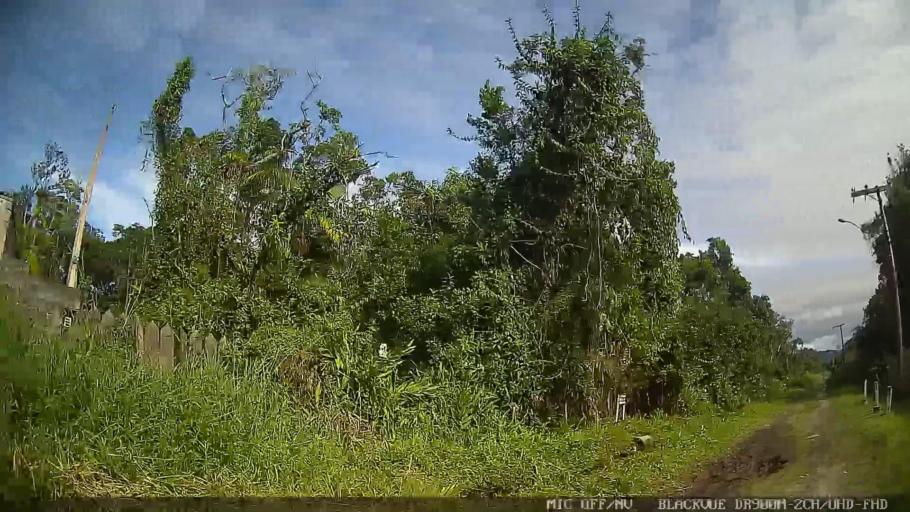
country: BR
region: Sao Paulo
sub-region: Peruibe
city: Peruibe
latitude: -24.2232
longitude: -46.9210
